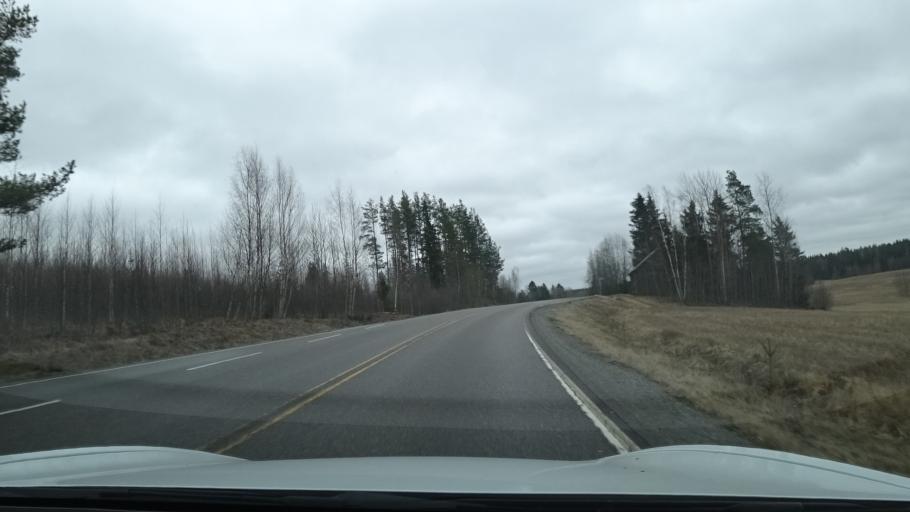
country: FI
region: Uusimaa
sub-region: Porvoo
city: Askola
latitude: 60.4965
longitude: 25.4969
